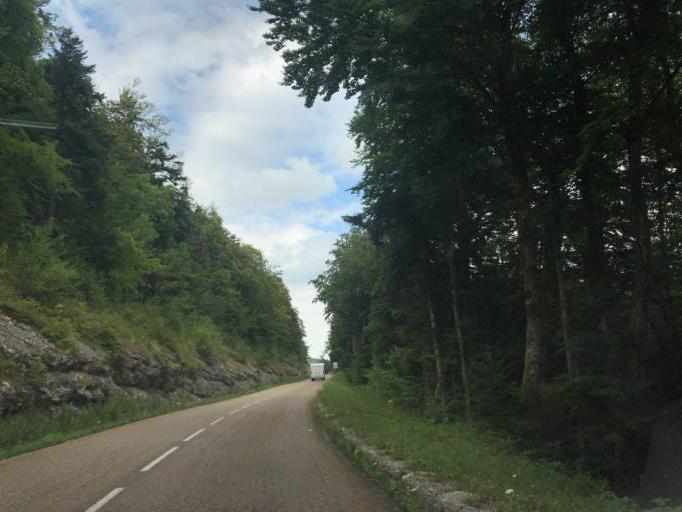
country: FR
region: Franche-Comte
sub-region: Departement du Jura
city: Longchaumois
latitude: 46.4936
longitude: 5.9210
